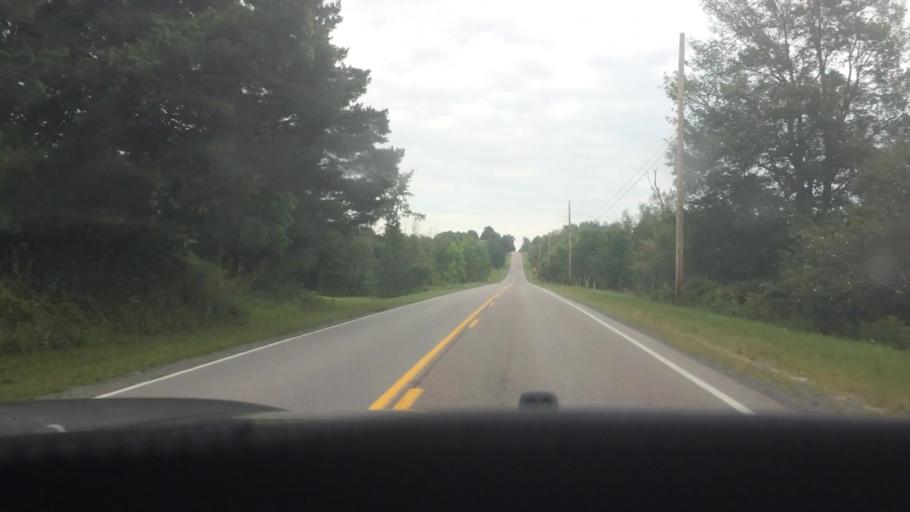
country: US
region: New York
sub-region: St. Lawrence County
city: Hannawa Falls
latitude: 44.5379
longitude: -75.0492
